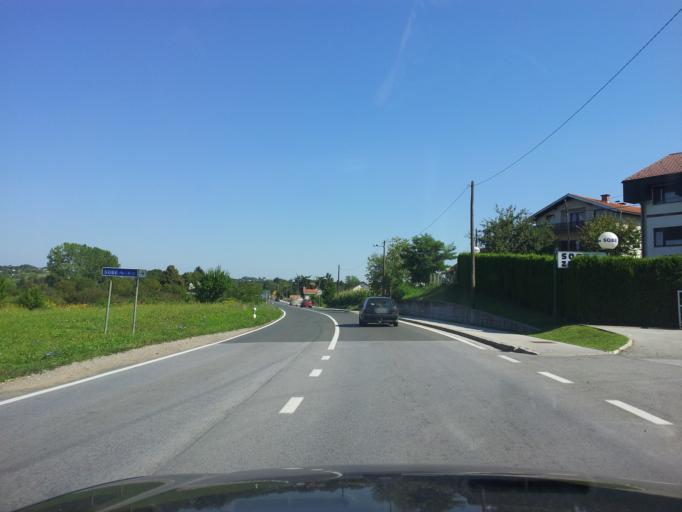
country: HR
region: Karlovacka
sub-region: Grad Karlovac
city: Karlovac
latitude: 45.4203
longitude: 15.6071
